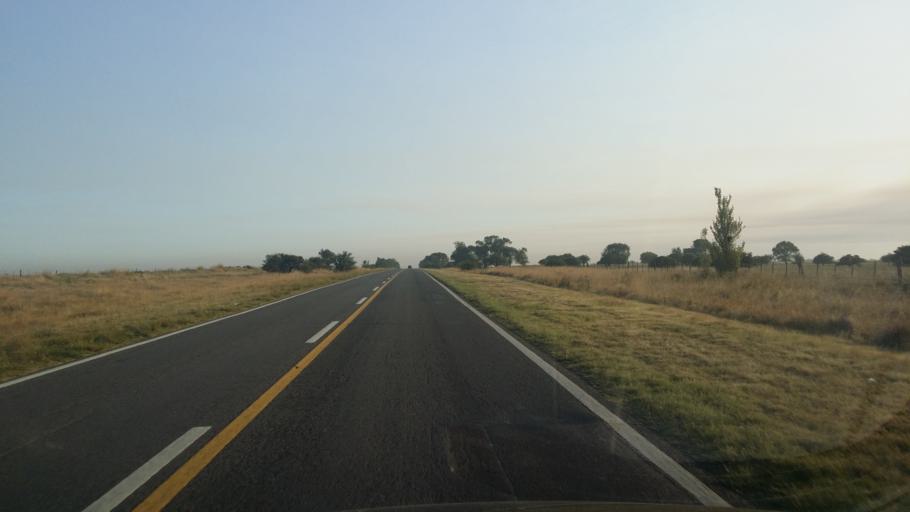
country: AR
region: La Pampa
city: Santa Rosa
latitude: -36.4510
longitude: -64.2799
